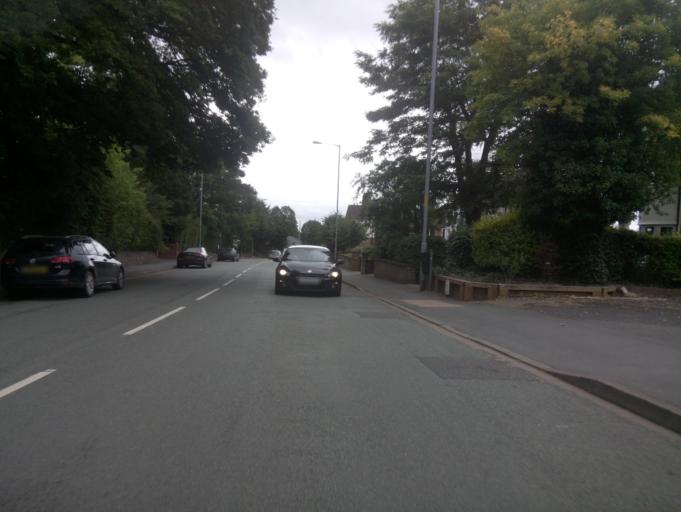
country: GB
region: England
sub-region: Worcestershire
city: Worcester
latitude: 52.1807
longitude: -2.2167
